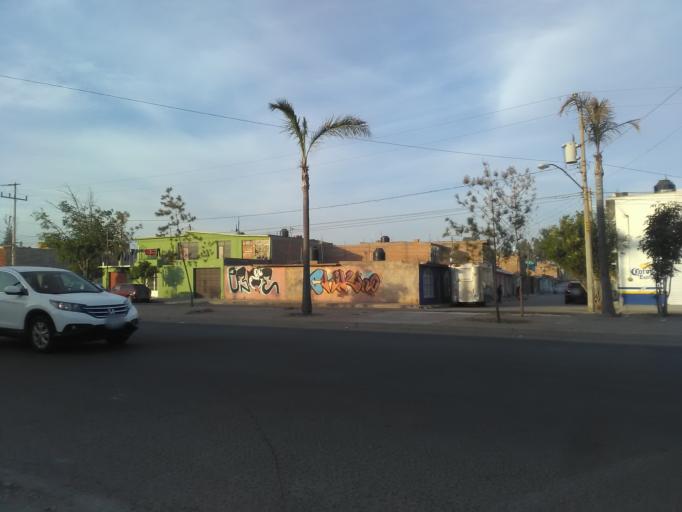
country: MX
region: Durango
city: Victoria de Durango
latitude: 24.0529
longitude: -104.6428
